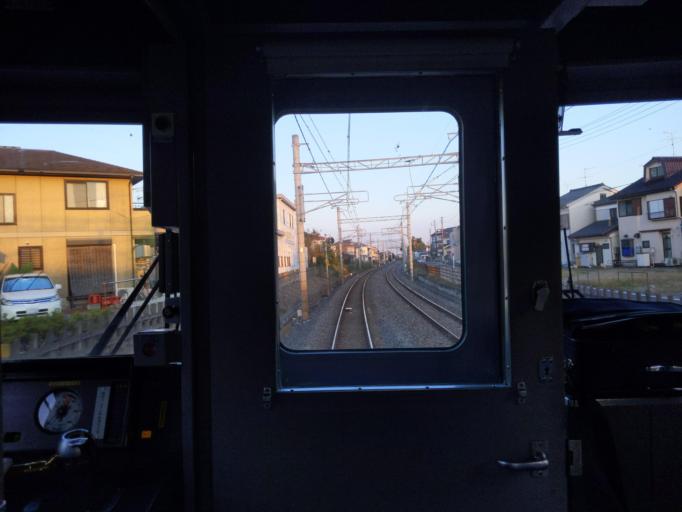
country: JP
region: Chiba
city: Noda
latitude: 35.9812
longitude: 139.8155
